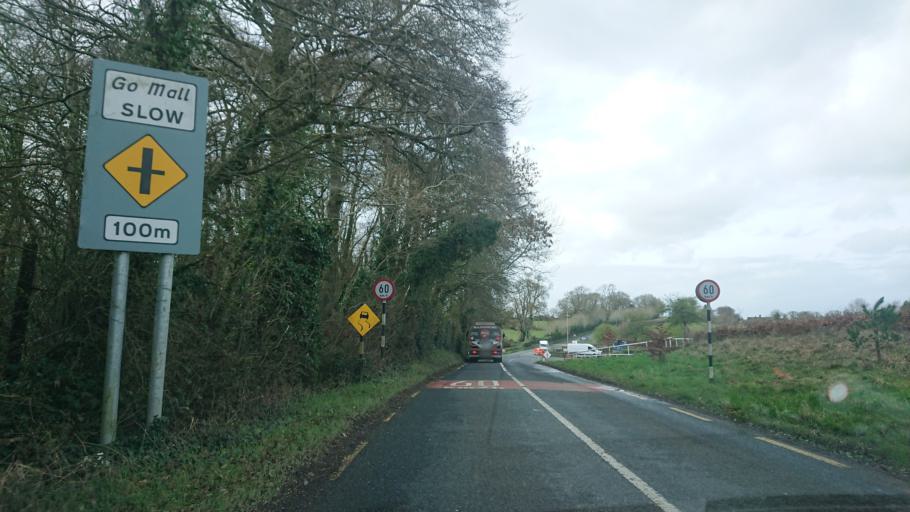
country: IE
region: Leinster
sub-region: Kildare
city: Naas
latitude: 53.1865
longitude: -6.6409
